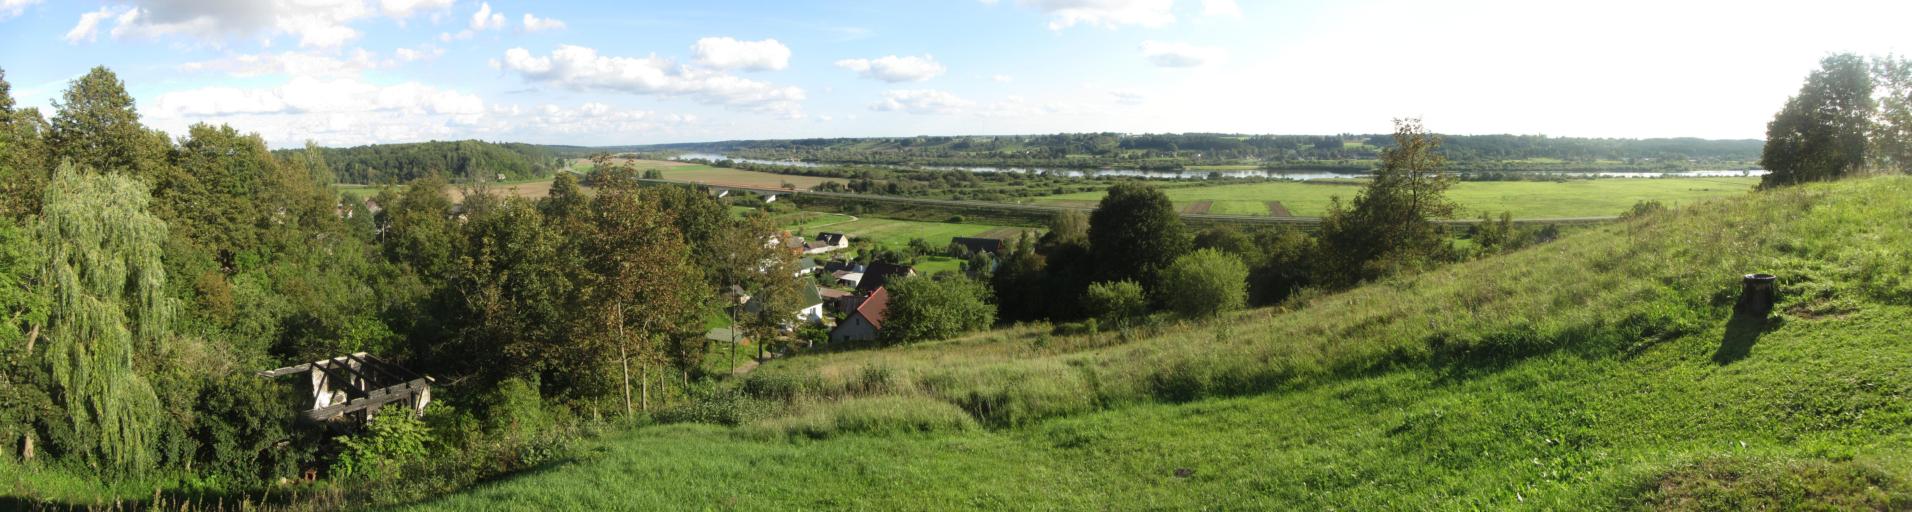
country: LT
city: Vilkija
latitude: 55.0808
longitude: 23.4157
